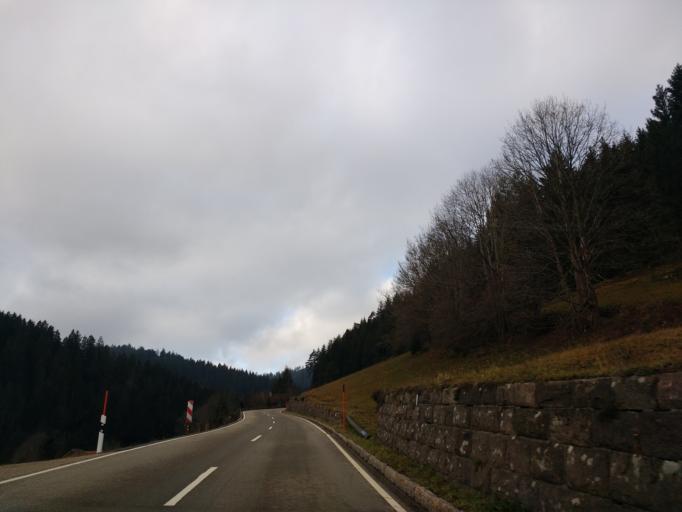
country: DE
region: Baden-Wuerttemberg
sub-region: Karlsruhe Region
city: Bad Rippoldsau-Schapbach
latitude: 48.4479
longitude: 8.2971
